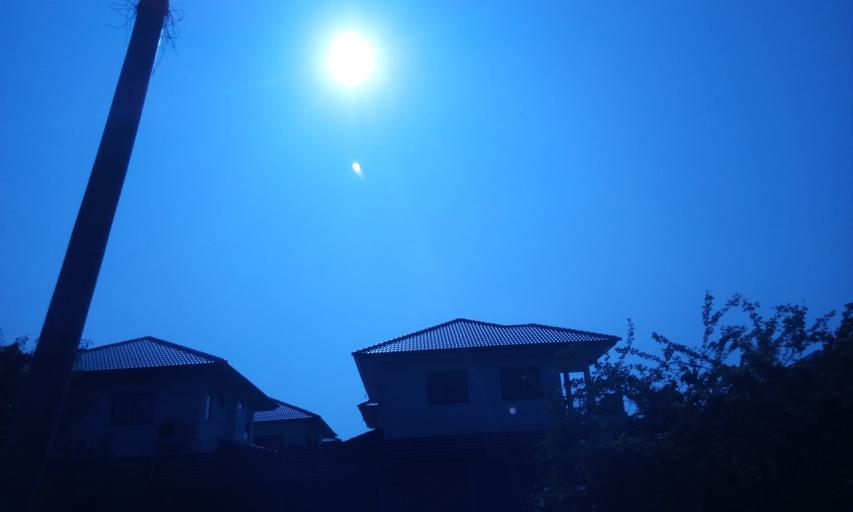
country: TH
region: Pathum Thani
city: Thanyaburi
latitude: 14.0044
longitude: 100.7088
